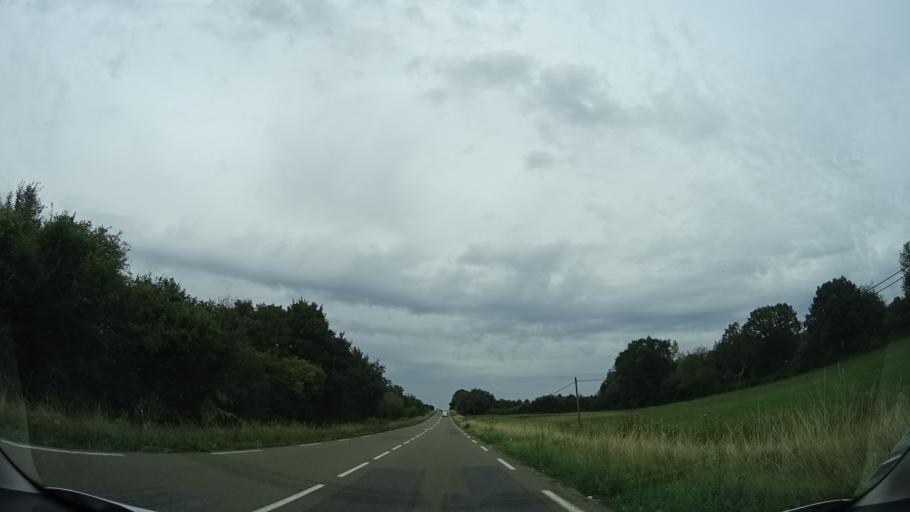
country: FR
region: Pays de la Loire
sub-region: Departement de la Mayenne
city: Entrammes
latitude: 48.0116
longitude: -0.6655
